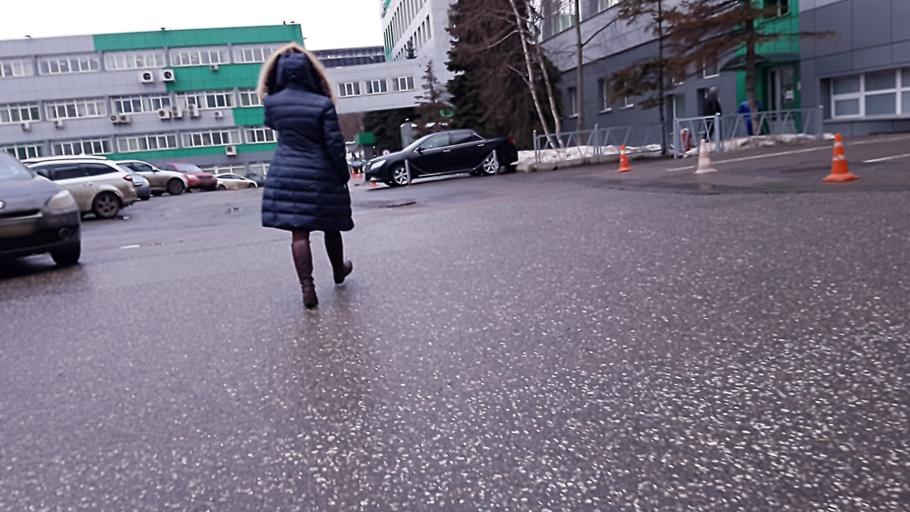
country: RU
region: Moscow
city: Kotlovka
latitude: 55.6888
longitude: 37.6148
